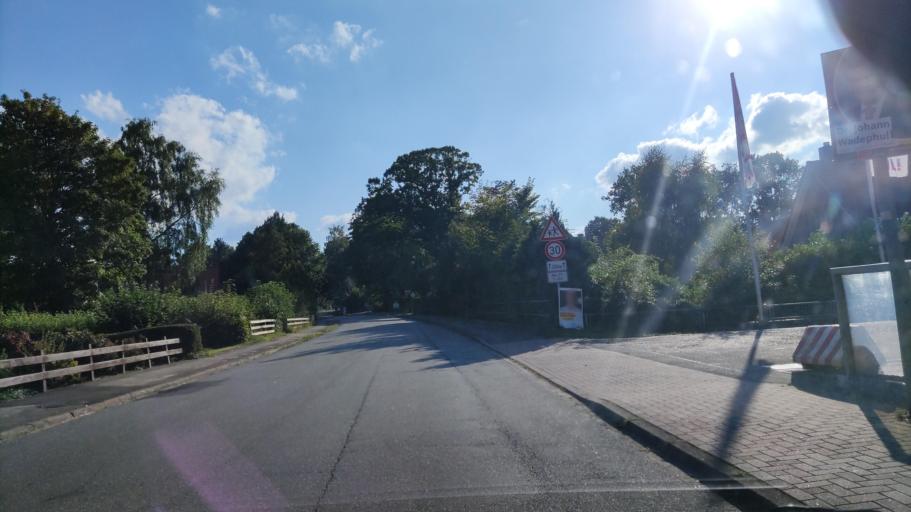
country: DE
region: Schleswig-Holstein
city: Aukrug
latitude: 54.0811
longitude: 9.7801
